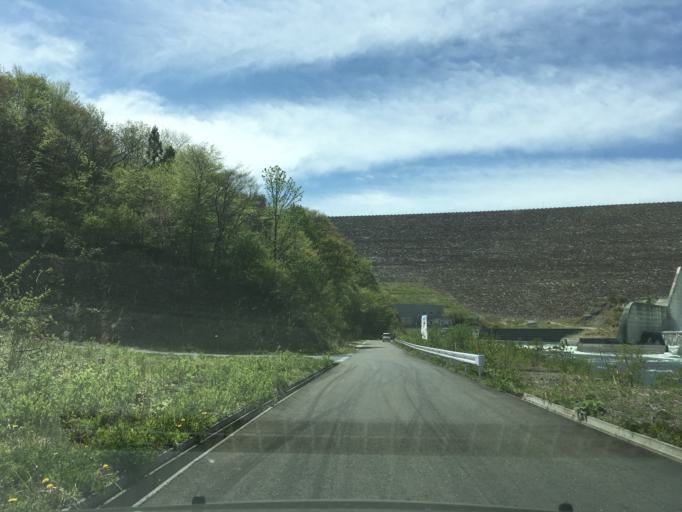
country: JP
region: Iwate
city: Mizusawa
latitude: 39.1222
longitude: 140.9269
